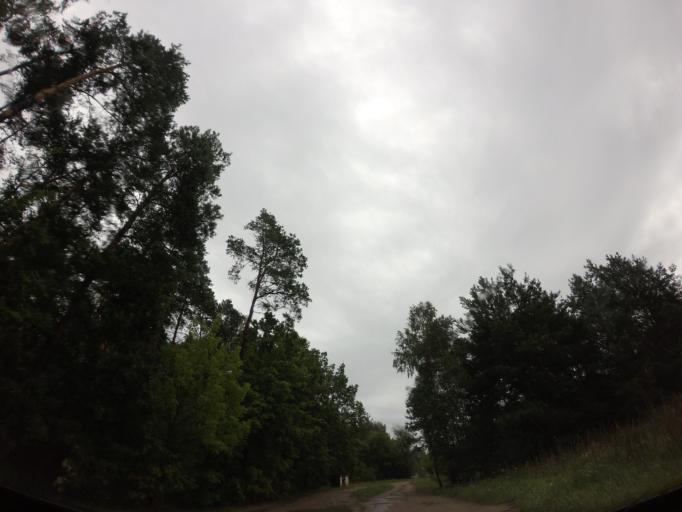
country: PL
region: Masovian Voivodeship
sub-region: Ostroleka
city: Ostroleka
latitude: 53.0831
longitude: 21.5440
